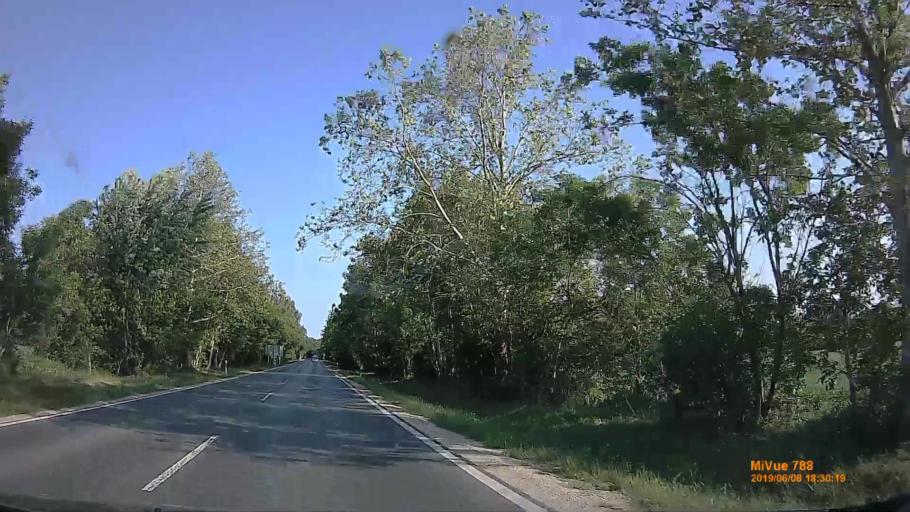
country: HU
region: Vas
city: Sarvar
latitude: 47.3756
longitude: 16.8840
